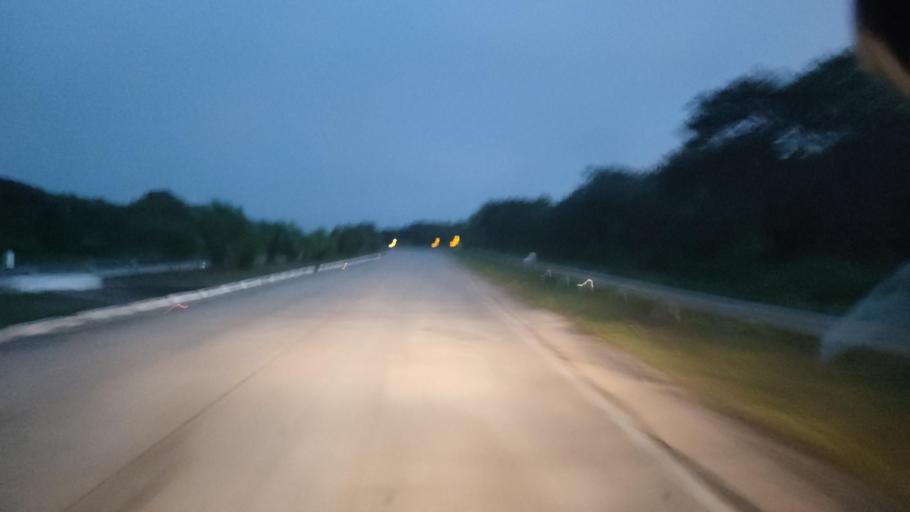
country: MM
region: Mandalay
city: Nay Pyi Taw
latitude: 20.0037
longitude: 95.9619
